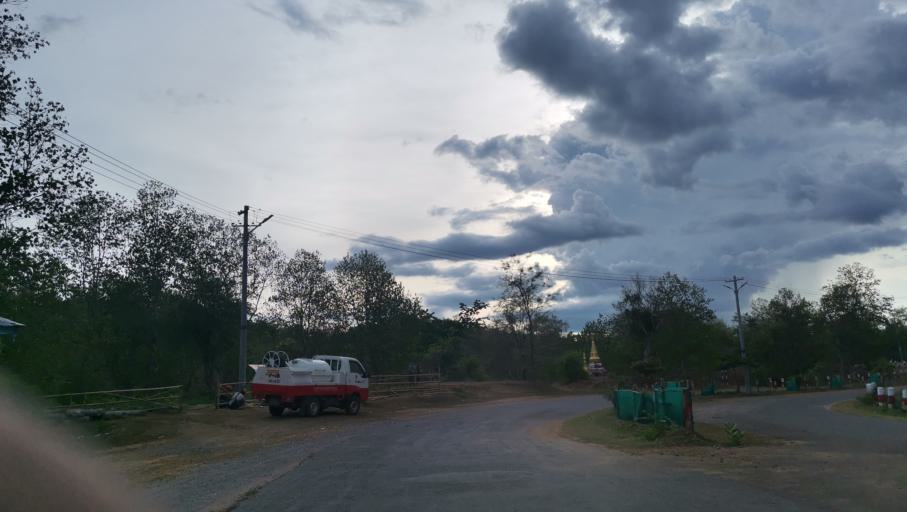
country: MM
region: Magway
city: Minbu
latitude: 20.0862
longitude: 94.5774
